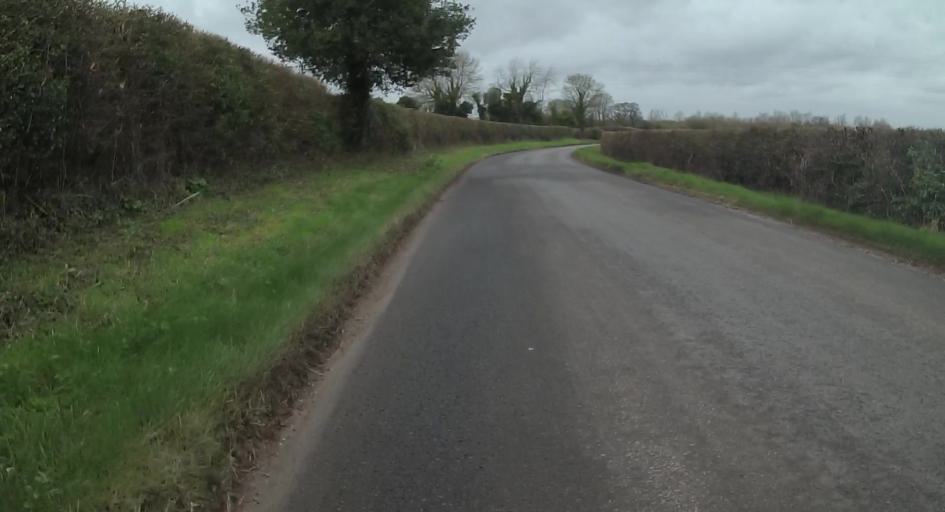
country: GB
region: England
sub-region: Hampshire
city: Kingsclere
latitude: 51.3267
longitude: -1.2598
